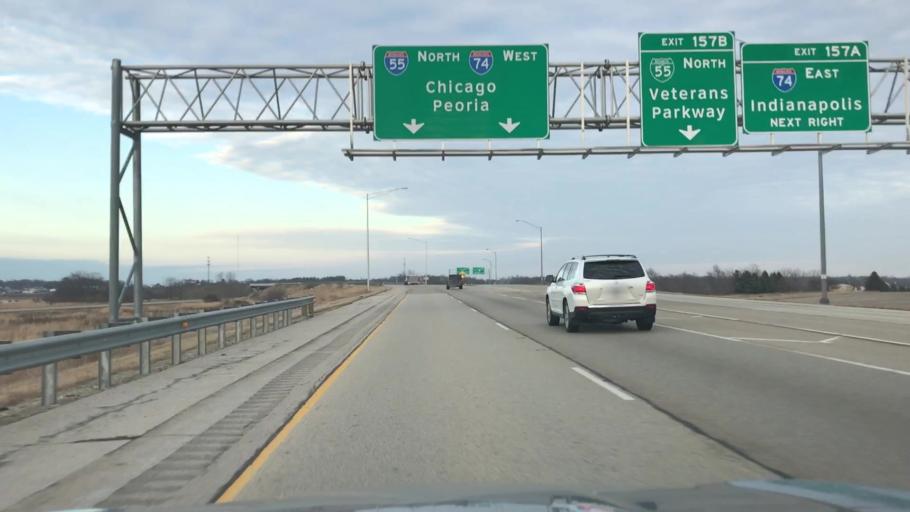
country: US
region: Illinois
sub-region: McLean County
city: Bloomington
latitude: 40.4359
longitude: -89.0274
